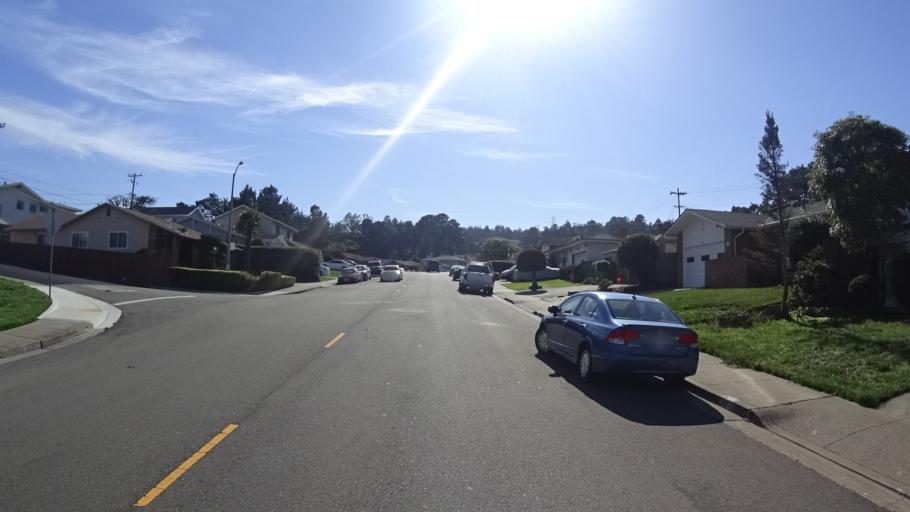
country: US
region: California
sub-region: San Mateo County
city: Colma
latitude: 37.6399
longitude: -122.4544
